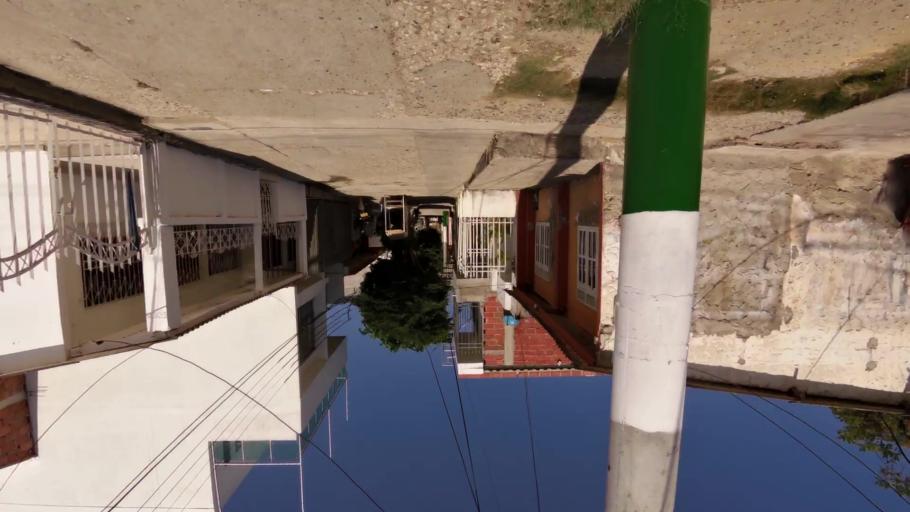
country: CO
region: Bolivar
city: Cartagena
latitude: 10.3924
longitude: -75.5087
